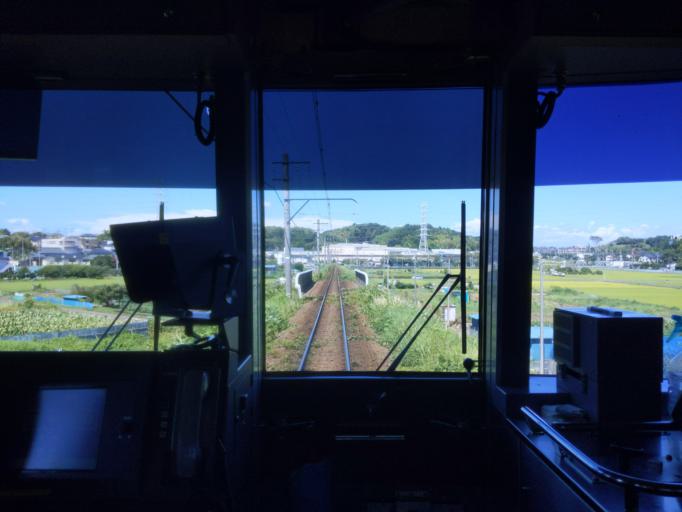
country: JP
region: Tokyo
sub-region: Machida-shi
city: Machida
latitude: 35.5389
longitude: 139.4930
